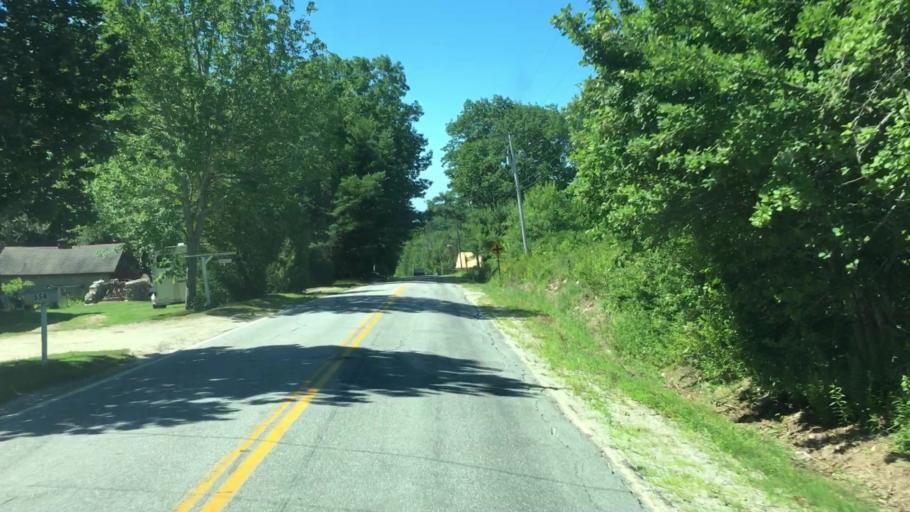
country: US
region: Maine
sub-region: Hancock County
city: Sedgwick
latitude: 44.3189
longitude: -68.6106
